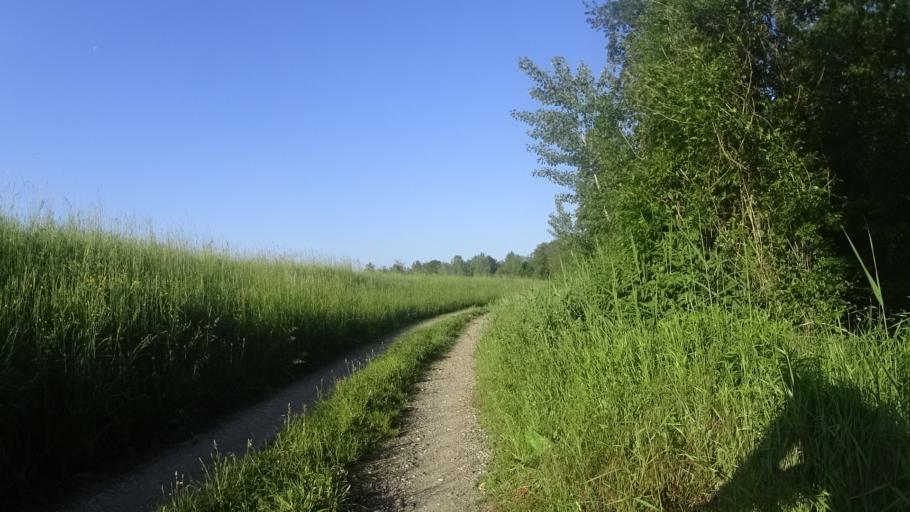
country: DE
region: Baden-Wuerttemberg
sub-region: Freiburg Region
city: Rheinau
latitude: 48.6988
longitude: 7.9546
